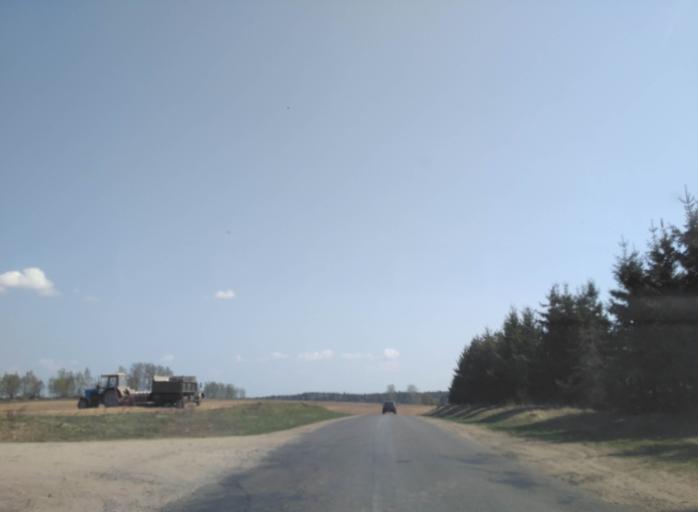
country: BY
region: Minsk
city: Horad Barysaw
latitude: 54.3143
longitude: 28.5505
